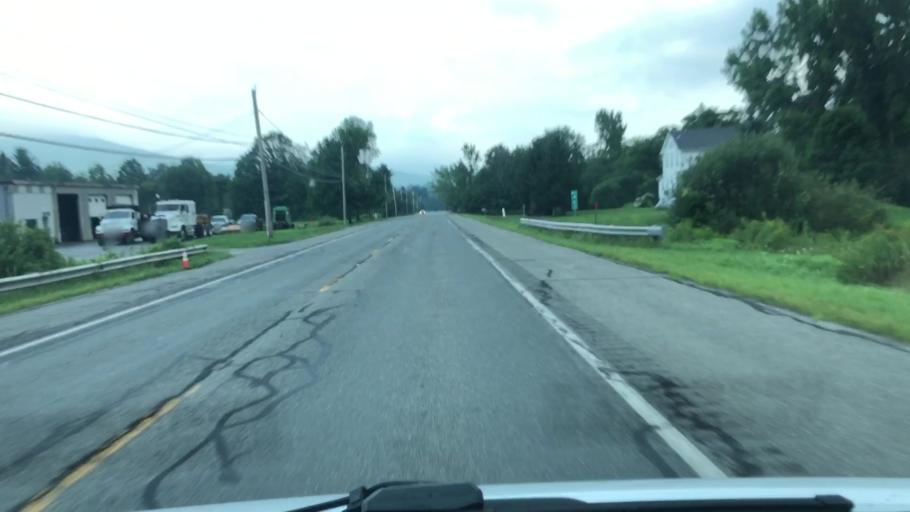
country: US
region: Massachusetts
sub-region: Berkshire County
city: Williamstown
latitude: 42.6502
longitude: -73.2370
